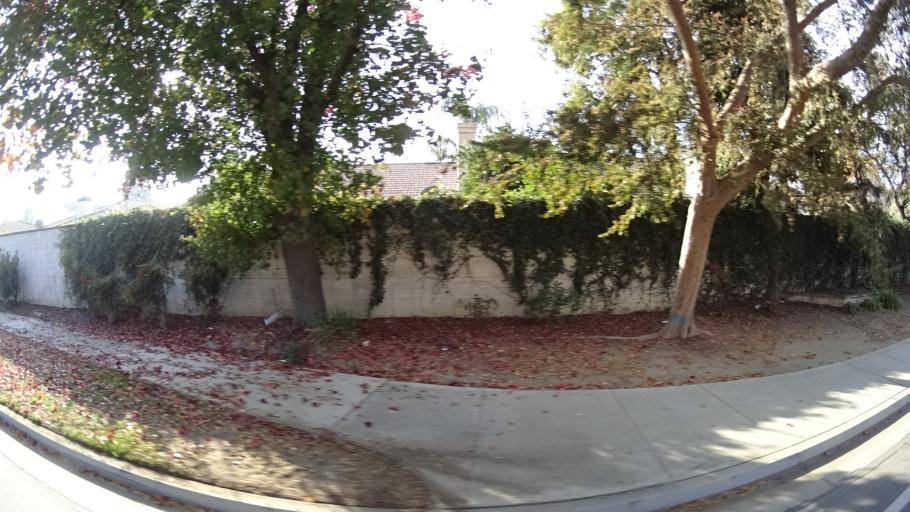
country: US
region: California
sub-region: Kern County
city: Greenacres
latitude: 35.3688
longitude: -119.1065
